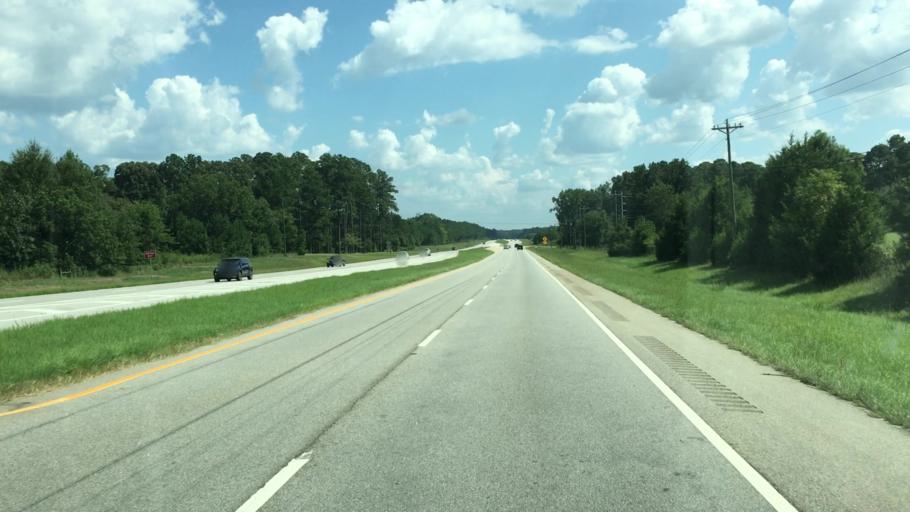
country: US
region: Georgia
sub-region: Putnam County
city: Eatonton
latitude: 33.2630
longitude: -83.3337
